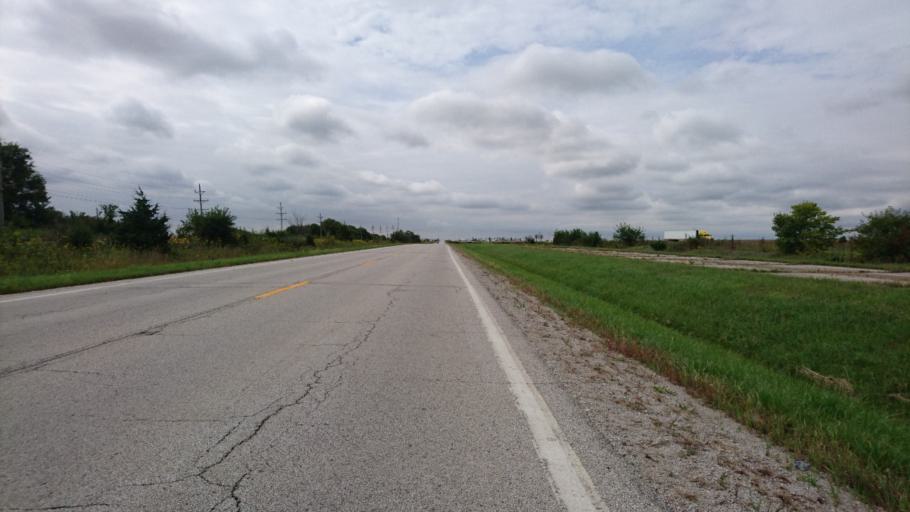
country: US
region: Illinois
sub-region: Livingston County
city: Odell
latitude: 40.9873
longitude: -88.5403
